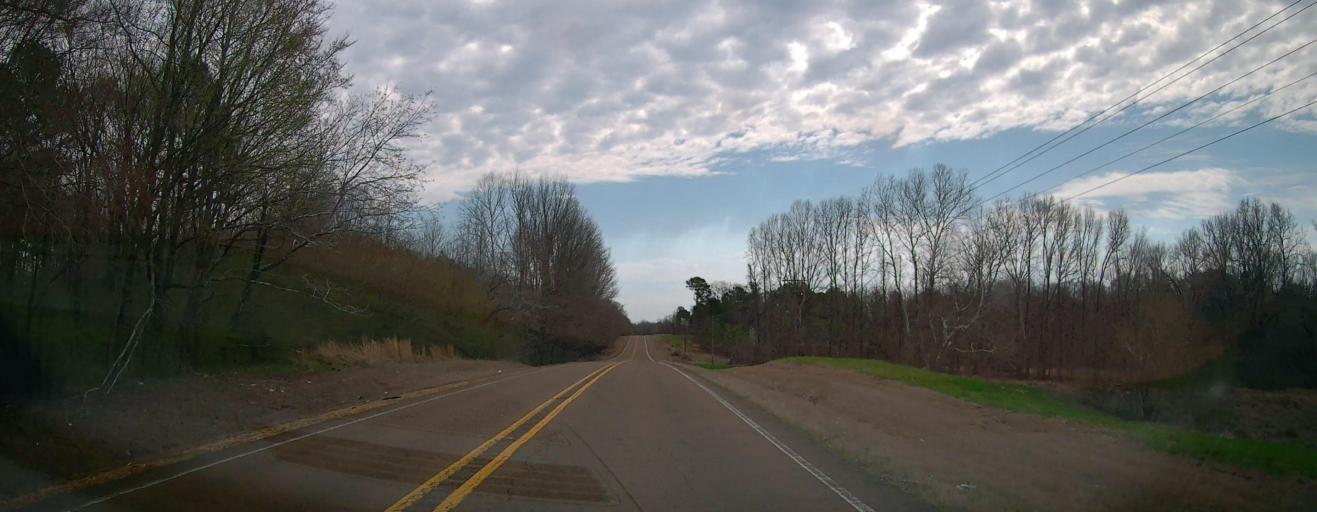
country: US
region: Mississippi
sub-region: Marshall County
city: Byhalia
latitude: 34.8525
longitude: -89.6359
